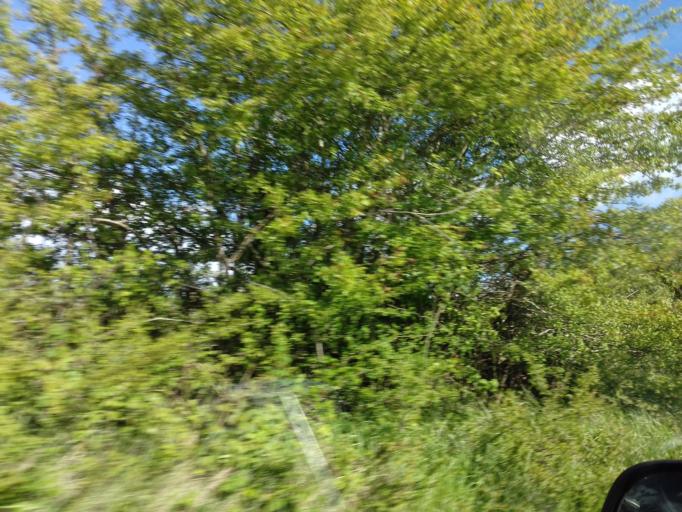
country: IE
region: Leinster
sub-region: Loch Garman
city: Castlebridge
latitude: 52.3909
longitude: -6.4042
